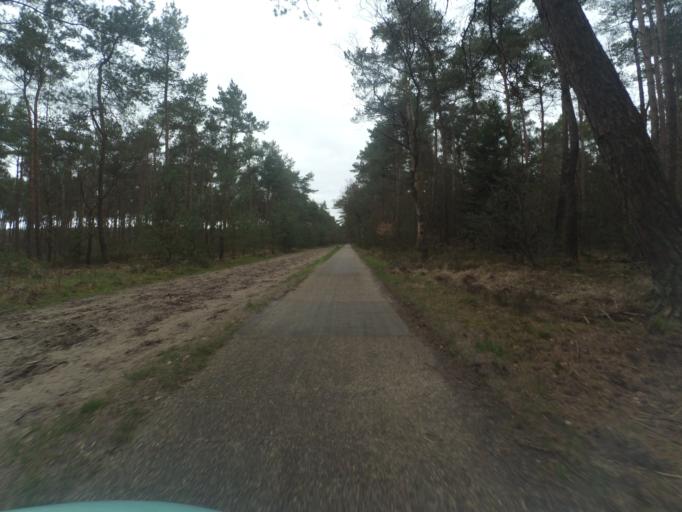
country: NL
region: Gelderland
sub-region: Gemeente Apeldoorn
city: Loenen
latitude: 52.0915
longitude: 6.0202
